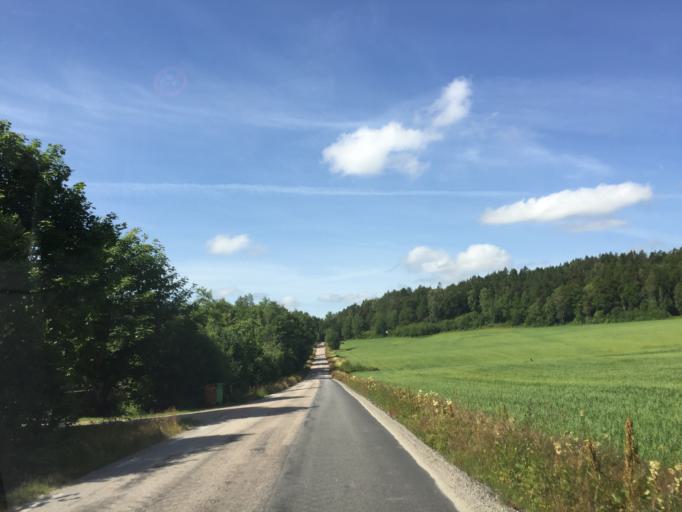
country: SE
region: Vaestra Goetaland
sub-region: Orust
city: Henan
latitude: 58.2919
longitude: 11.6348
